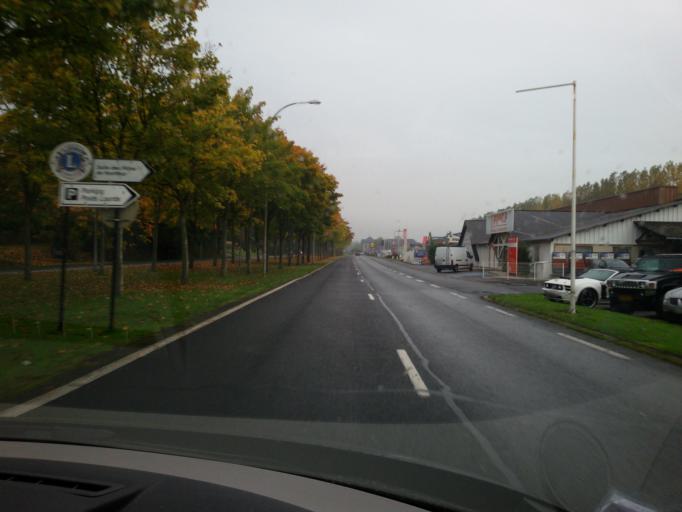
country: FR
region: Lower Normandy
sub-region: Departement du Calvados
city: Honfleur
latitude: 49.4137
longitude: 0.2489
